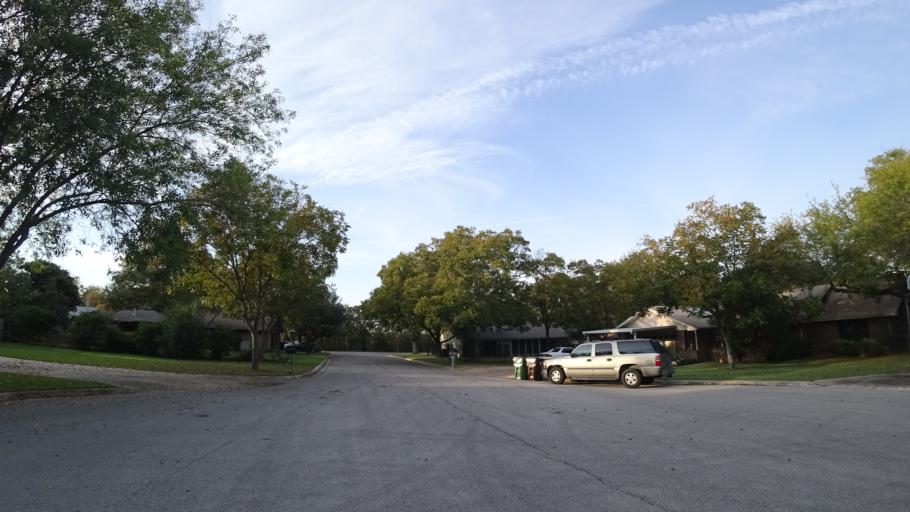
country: US
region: Texas
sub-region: Williamson County
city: Round Rock
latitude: 30.5056
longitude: -97.6711
